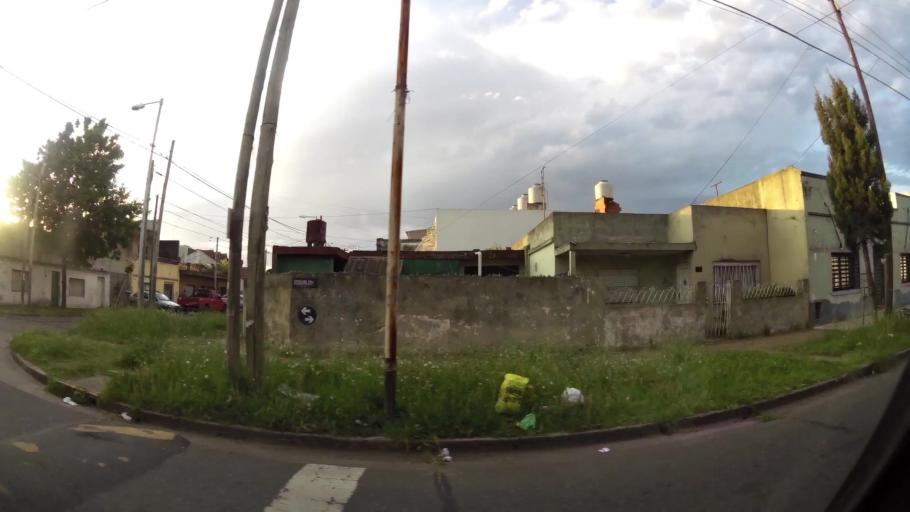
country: AR
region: Buenos Aires
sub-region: Partido de Avellaneda
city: Avellaneda
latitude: -34.7113
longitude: -58.3362
